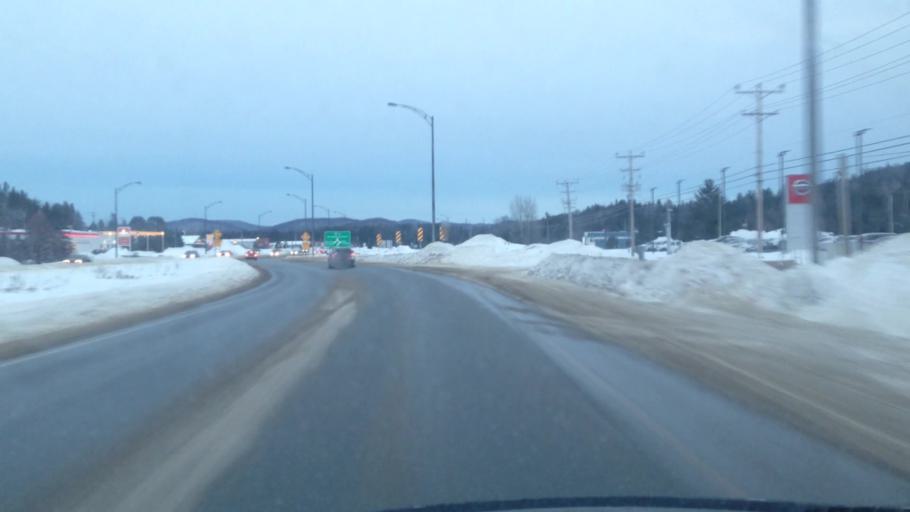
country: CA
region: Quebec
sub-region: Laurentides
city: Mont-Tremblant
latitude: 46.1163
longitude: -74.5673
